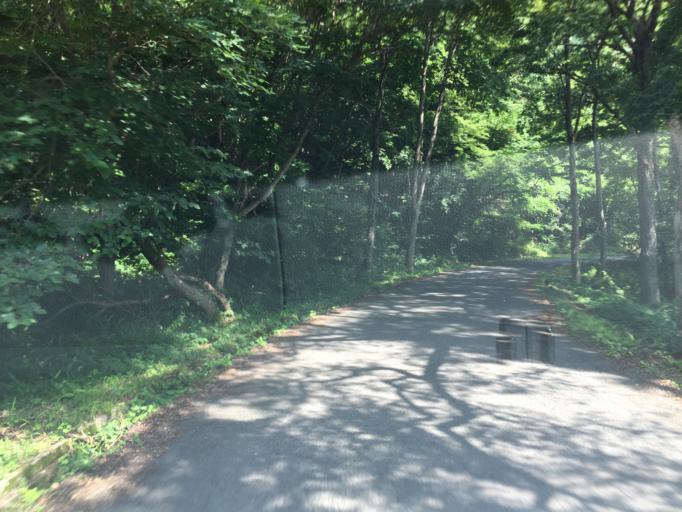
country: JP
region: Fukushima
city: Inawashiro
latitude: 37.4179
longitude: 140.0956
